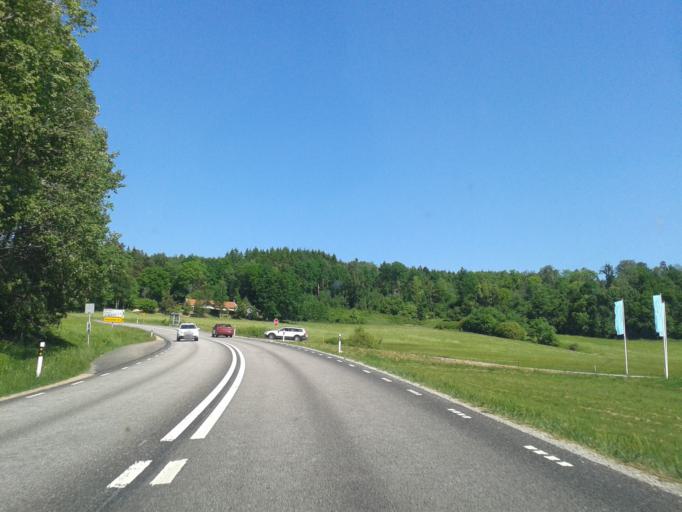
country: SE
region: Vaestra Goetaland
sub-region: Orust
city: Henan
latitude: 58.3272
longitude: 11.6887
